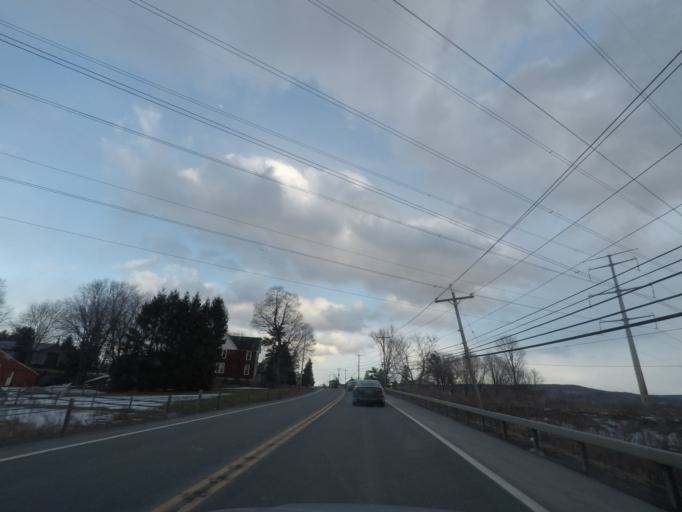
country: US
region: New York
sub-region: Oneida County
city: Utica
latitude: 43.1028
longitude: -75.1603
